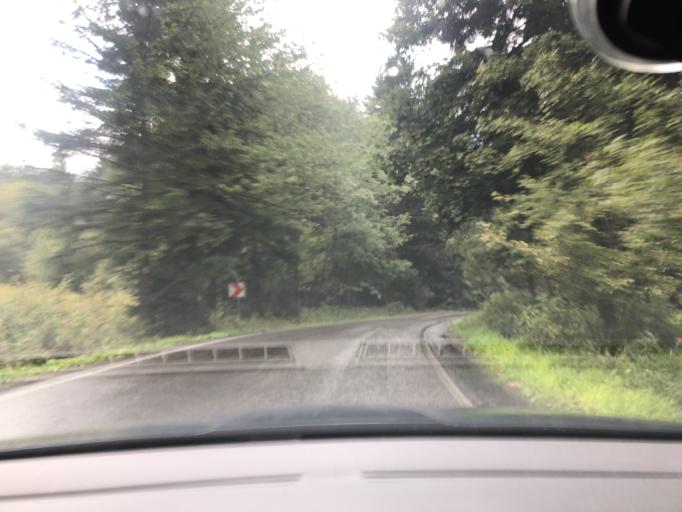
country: PL
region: Lesser Poland Voivodeship
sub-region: Powiat suski
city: Zawoja
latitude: 49.6856
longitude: 19.5592
